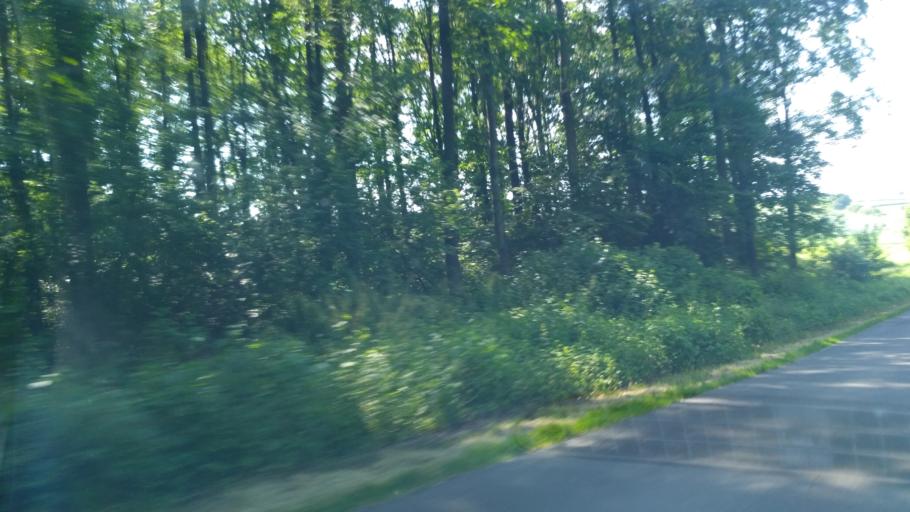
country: PL
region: Subcarpathian Voivodeship
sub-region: Powiat jaroslawski
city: Rokietnica
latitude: 49.9305
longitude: 22.6754
